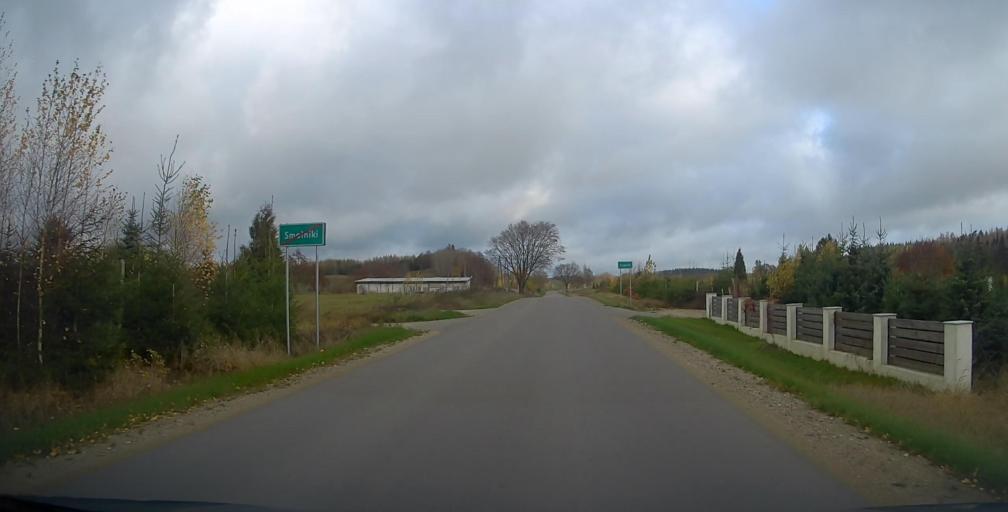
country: PL
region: Podlasie
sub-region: Suwalki
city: Suwalki
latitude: 54.2945
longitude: 22.8786
